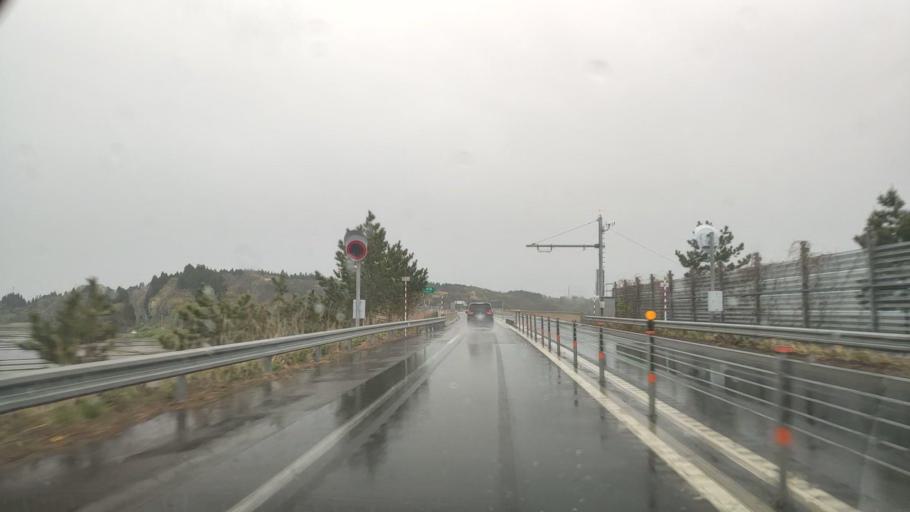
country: JP
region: Akita
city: Noshiromachi
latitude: 40.1790
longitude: 140.0605
